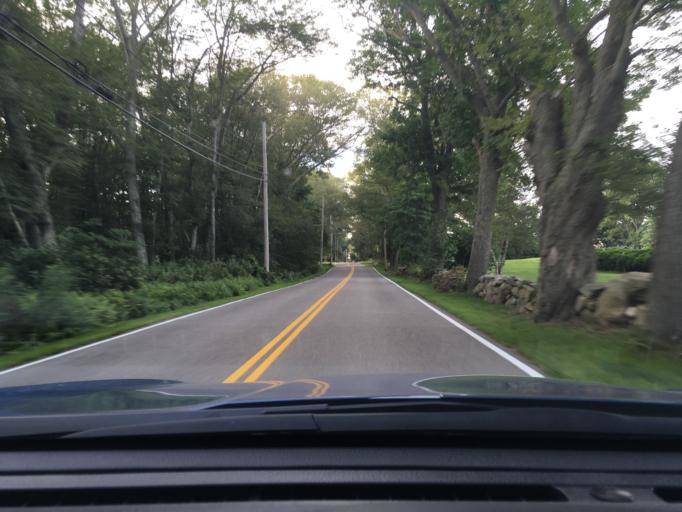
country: US
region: Rhode Island
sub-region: Washington County
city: Exeter
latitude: 41.6179
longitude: -71.5098
